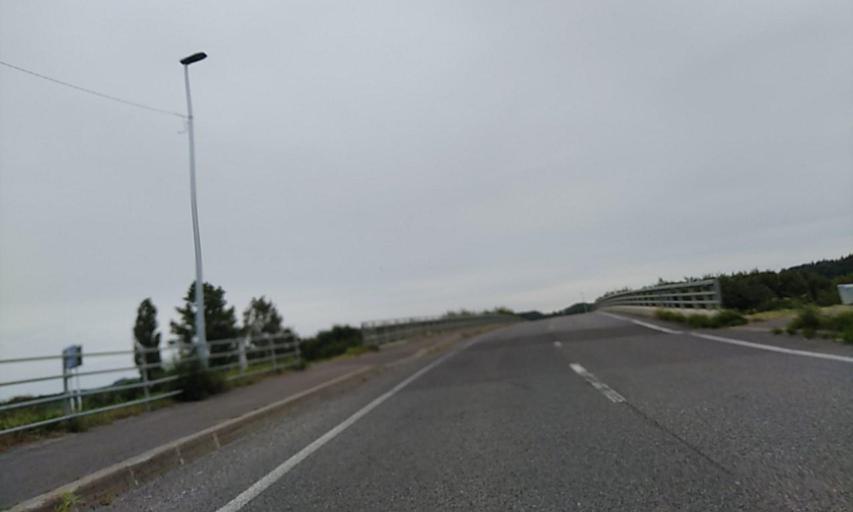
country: JP
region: Hokkaido
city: Bihoro
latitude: 43.8387
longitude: 144.1127
